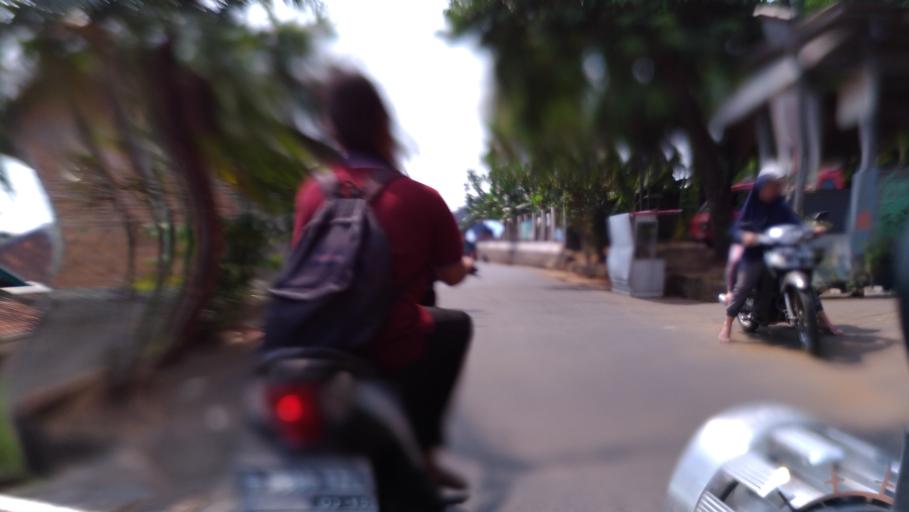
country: ID
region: West Java
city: Depok
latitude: -6.3567
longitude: 106.8746
